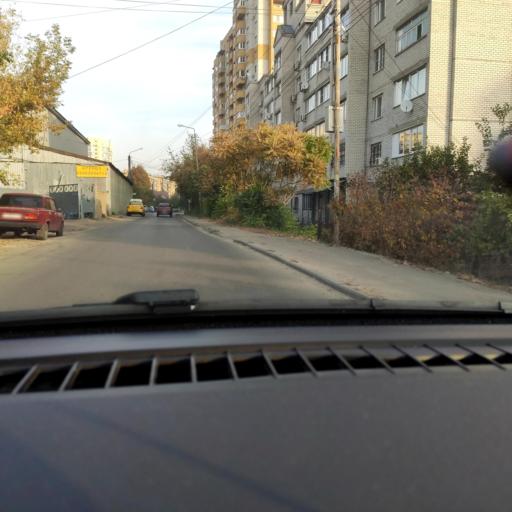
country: RU
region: Voronezj
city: Voronezh
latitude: 51.6999
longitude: 39.2041
